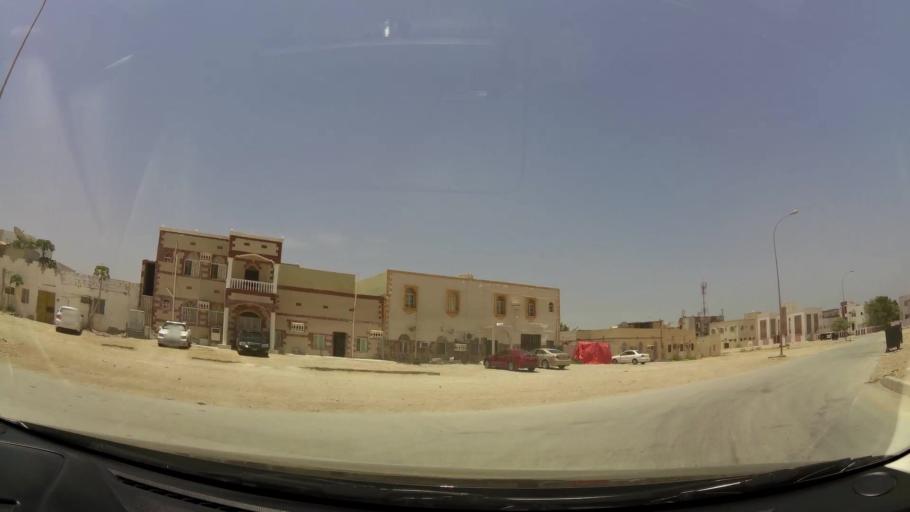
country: OM
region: Zufar
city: Salalah
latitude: 17.0800
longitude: 54.1522
